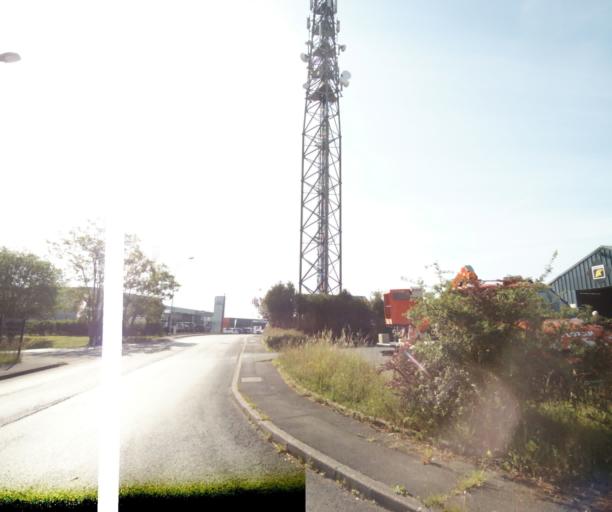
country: FR
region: Champagne-Ardenne
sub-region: Departement des Ardennes
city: La Francheville
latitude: 49.7395
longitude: 4.7014
